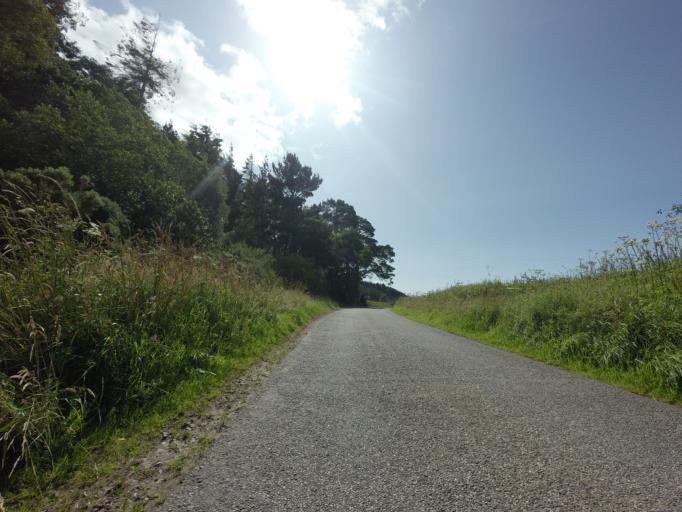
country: GB
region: Scotland
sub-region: Highland
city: Nairn
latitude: 57.5309
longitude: -3.8624
